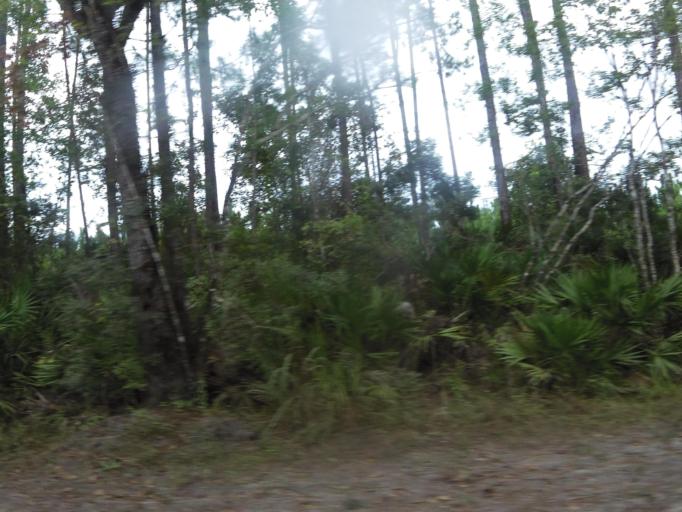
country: US
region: Florida
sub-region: Flagler County
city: Palm Coast
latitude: 29.6398
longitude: -81.3733
